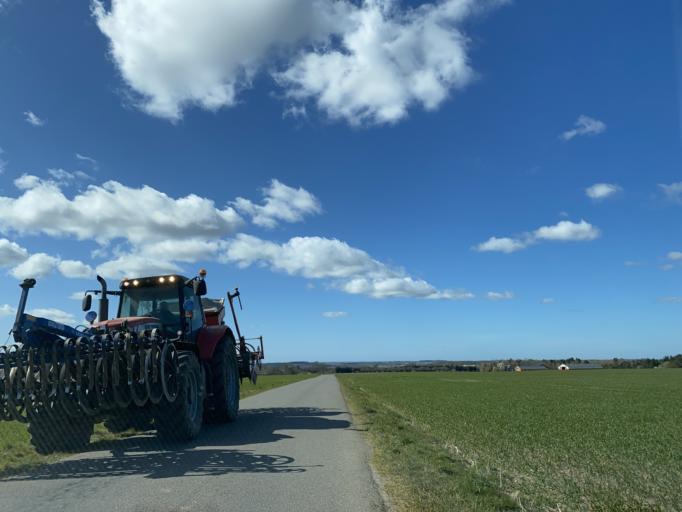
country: DK
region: Central Jutland
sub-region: Favrskov Kommune
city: Ulstrup
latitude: 56.3434
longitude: 9.8044
